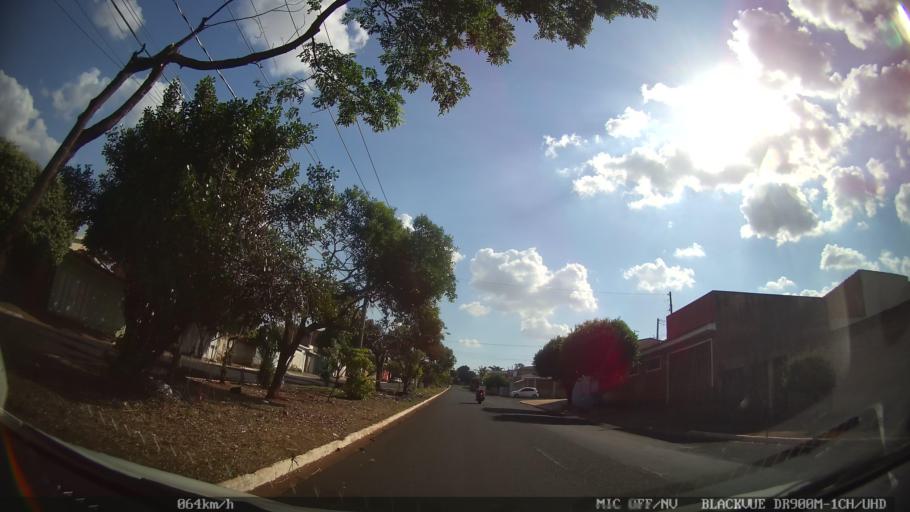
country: BR
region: Sao Paulo
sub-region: Ribeirao Preto
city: Ribeirao Preto
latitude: -21.1966
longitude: -47.8366
